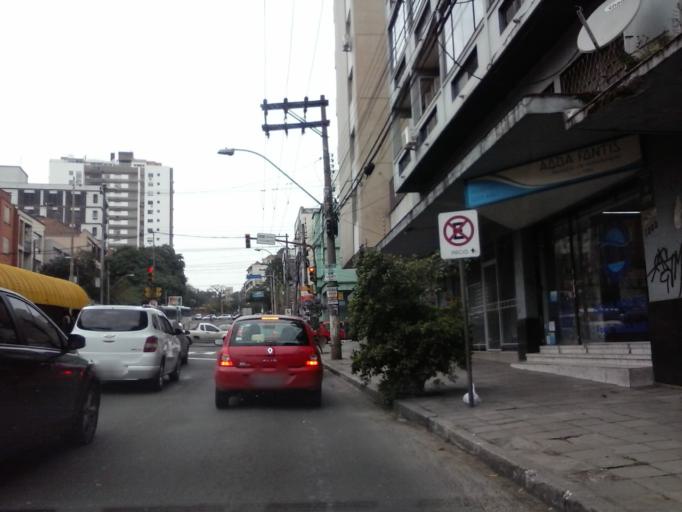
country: BR
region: Rio Grande do Sul
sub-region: Porto Alegre
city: Porto Alegre
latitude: -30.0403
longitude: -51.1964
